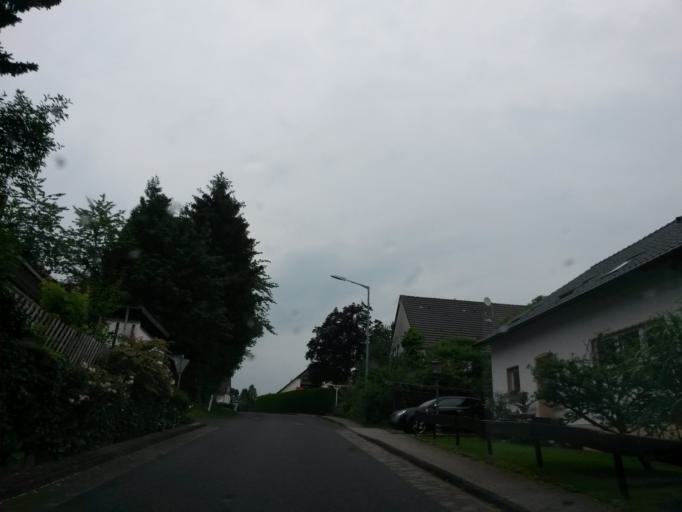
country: DE
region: North Rhine-Westphalia
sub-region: Regierungsbezirk Koln
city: Overath
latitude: 50.8961
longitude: 7.3369
